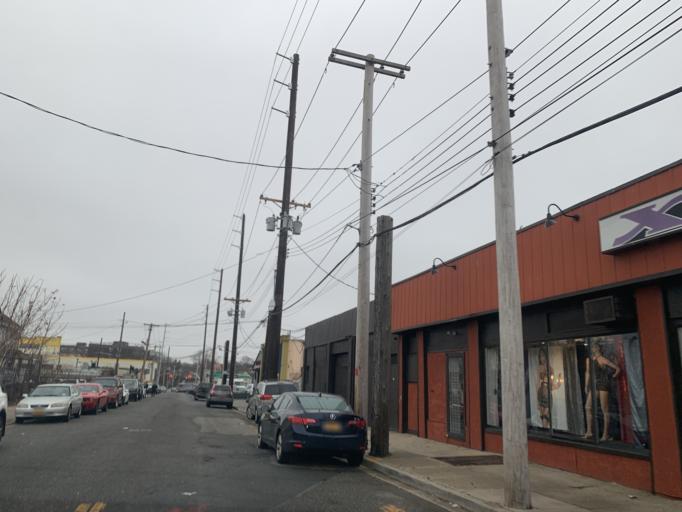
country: US
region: New York
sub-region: Nassau County
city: Hempstead
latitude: 40.7127
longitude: -73.6267
